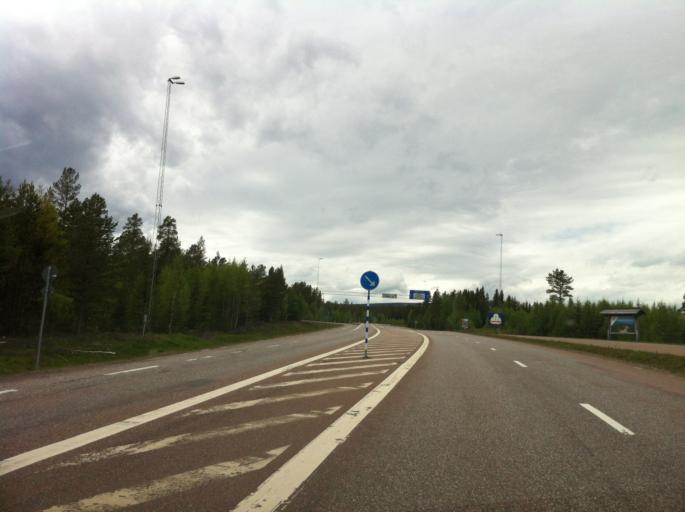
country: SE
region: Dalarna
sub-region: Malung-Saelens kommun
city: Malung
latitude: 61.1655
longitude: 13.2604
